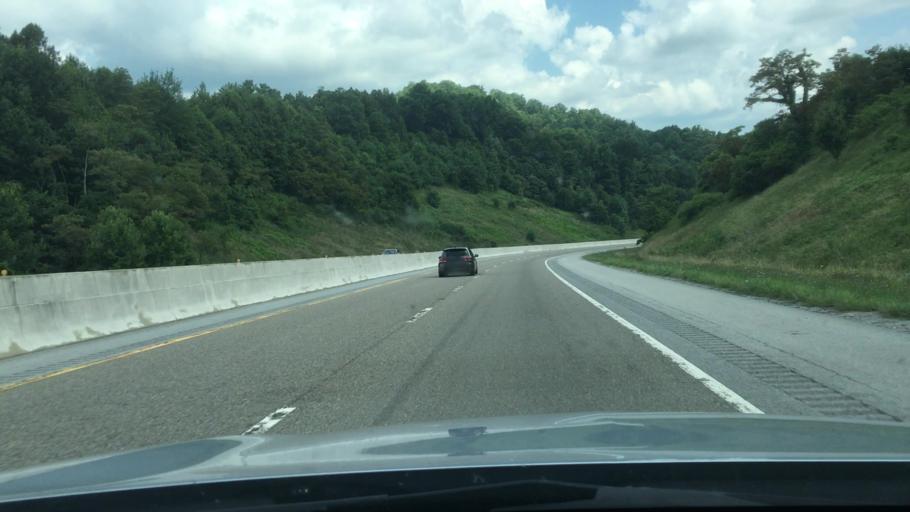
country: US
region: North Carolina
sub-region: Madison County
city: Mars Hill
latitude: 35.9945
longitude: -82.5441
